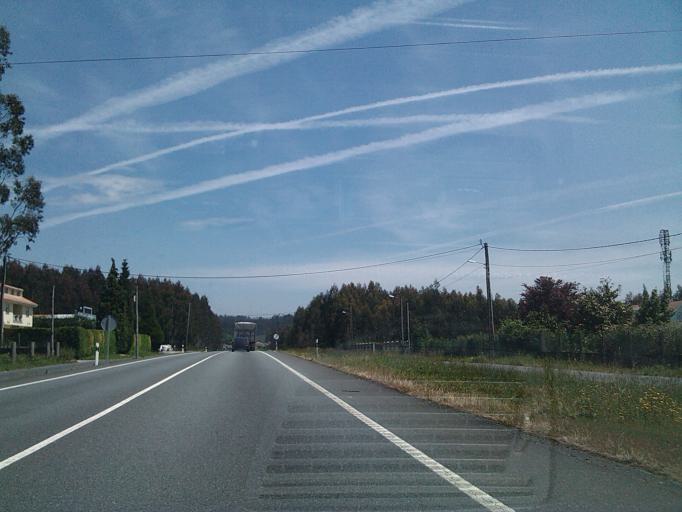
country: ES
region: Galicia
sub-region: Provincia da Coruna
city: Oroso
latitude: 42.9178
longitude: -8.4109
